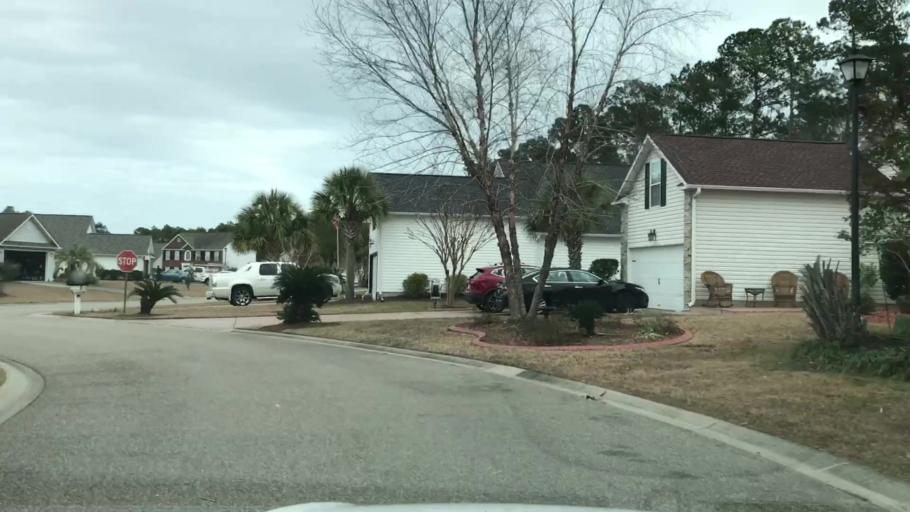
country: US
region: South Carolina
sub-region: Horry County
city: Socastee
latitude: 33.6692
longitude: -78.9741
